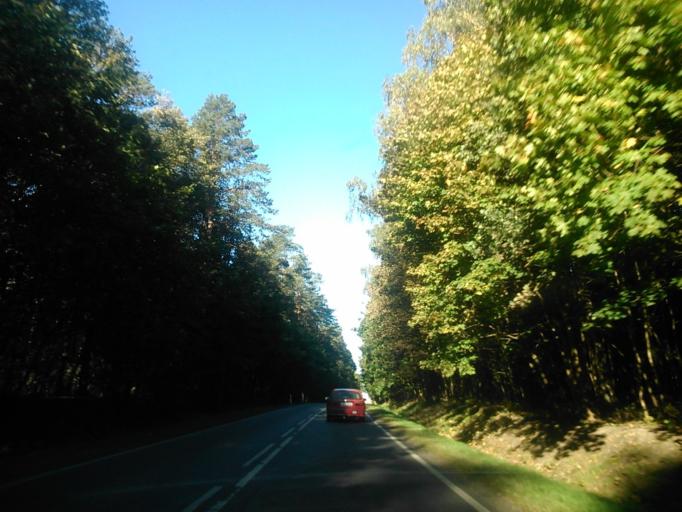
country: PL
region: Kujawsko-Pomorskie
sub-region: Powiat wabrzeski
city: Wabrzezno
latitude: 53.2601
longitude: 19.0059
